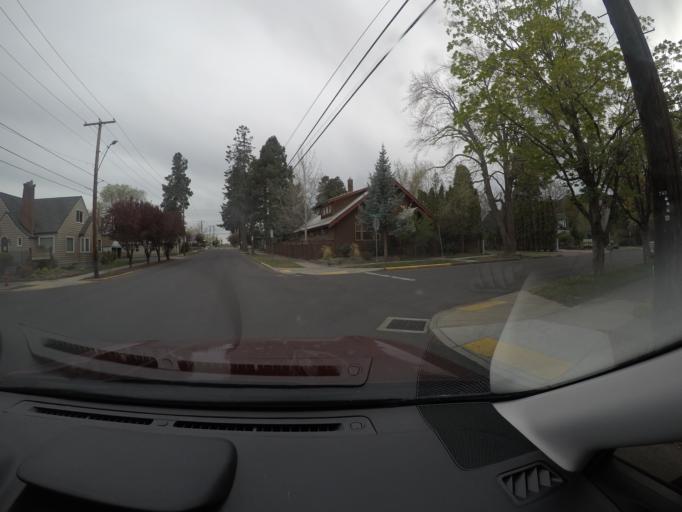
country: US
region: Oregon
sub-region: Deschutes County
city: Bend
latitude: 44.0571
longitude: -121.3089
